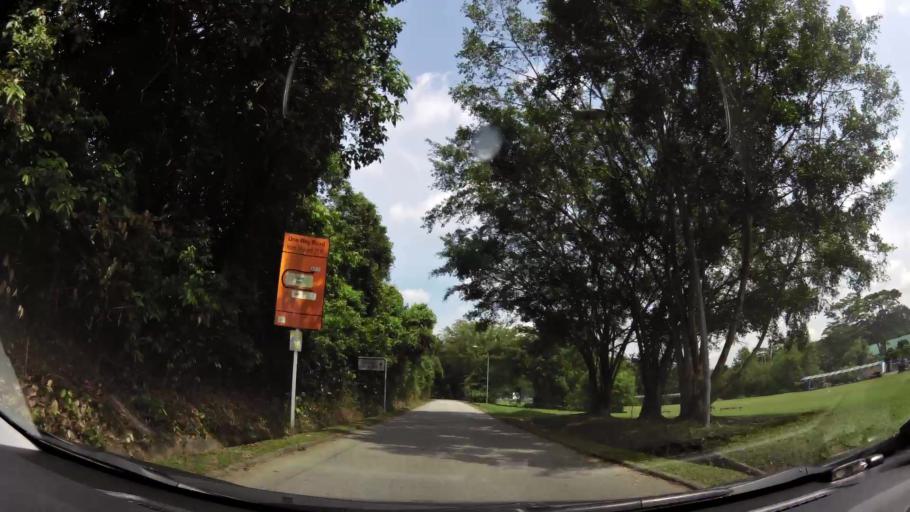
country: SG
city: Singapore
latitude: 1.3400
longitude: 103.7927
